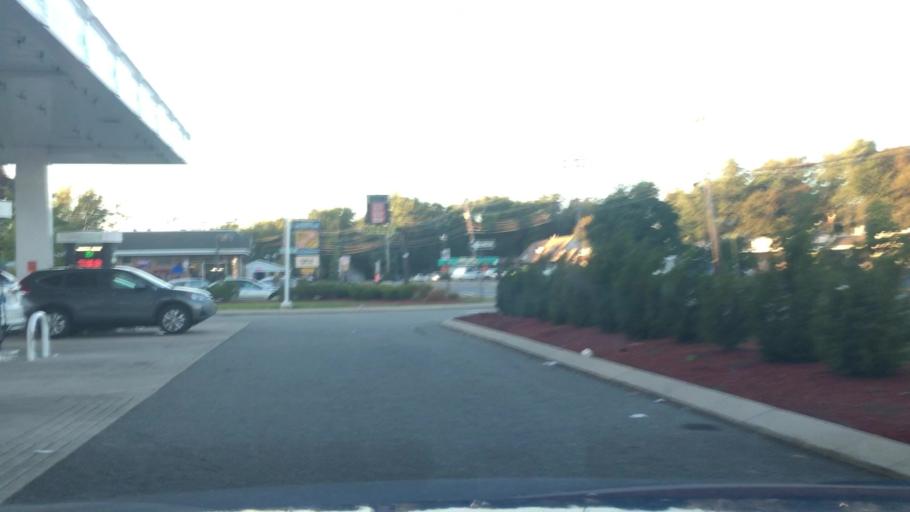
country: US
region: Massachusetts
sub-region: Middlesex County
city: Billerica
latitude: 42.5721
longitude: -71.2779
